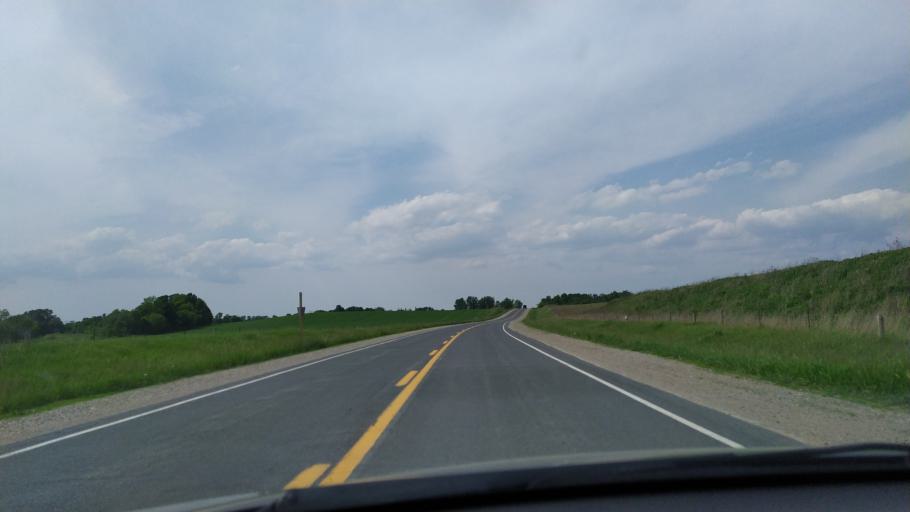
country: CA
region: Ontario
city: Ingersoll
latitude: 43.0151
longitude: -80.9653
